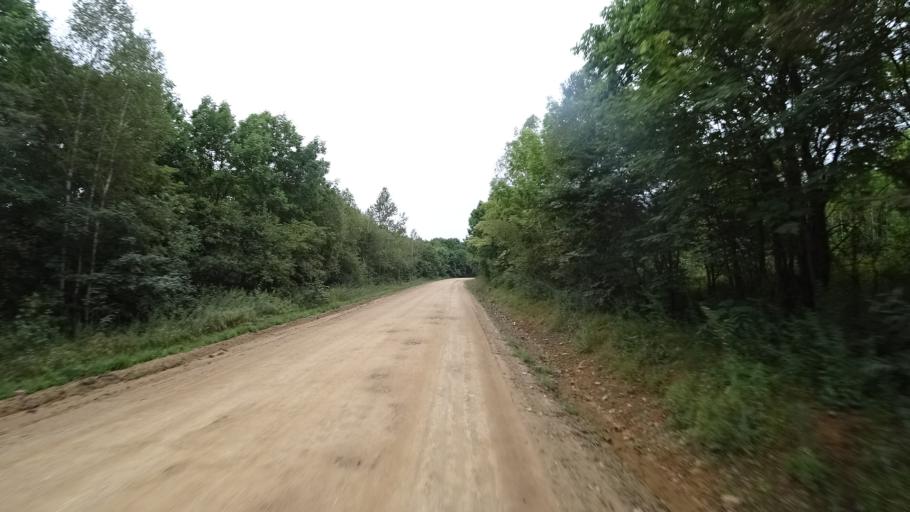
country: RU
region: Primorskiy
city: Rettikhovka
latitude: 44.1820
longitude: 132.8049
